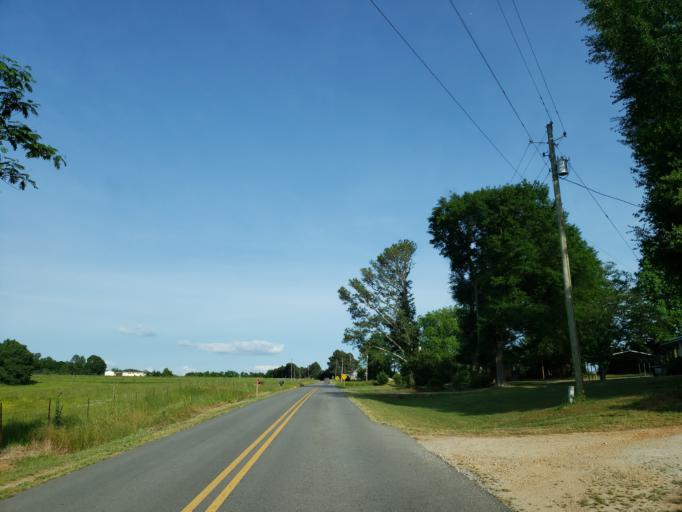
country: US
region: Georgia
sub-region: Carroll County
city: Bowdon
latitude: 33.5008
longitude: -85.3249
